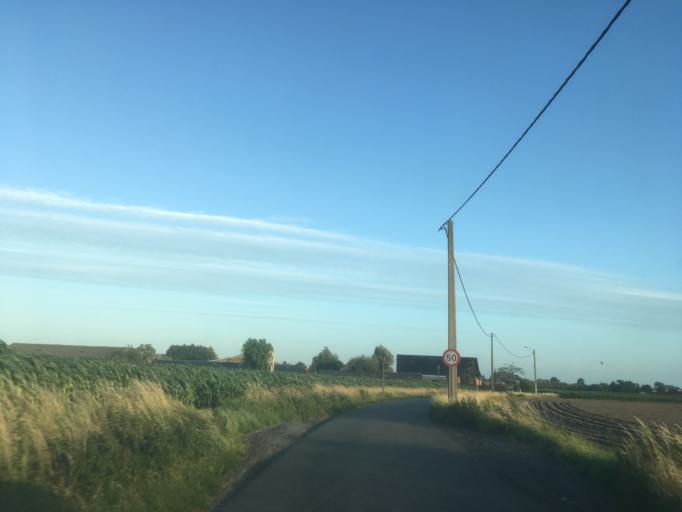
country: BE
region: Flanders
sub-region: Provincie West-Vlaanderen
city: Torhout
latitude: 51.0490
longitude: 3.0869
